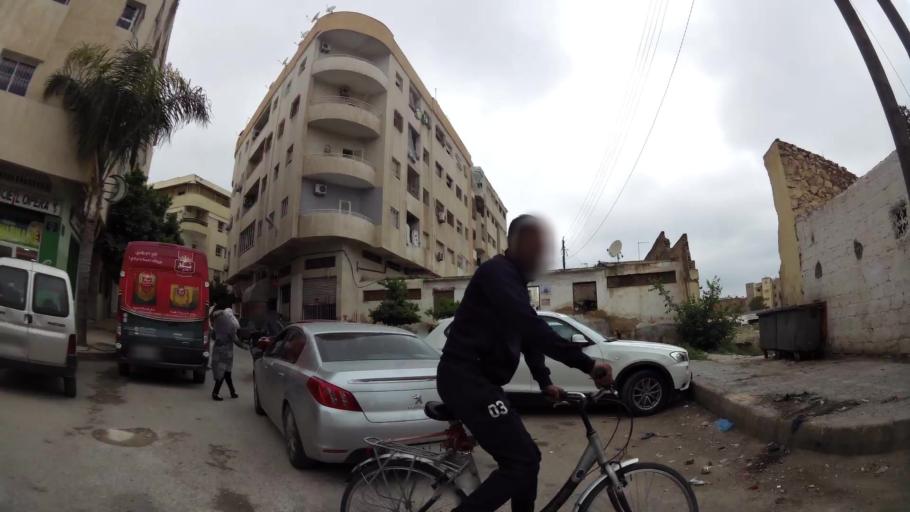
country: MA
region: Fes-Boulemane
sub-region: Fes
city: Fes
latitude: 34.0290
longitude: -4.9951
